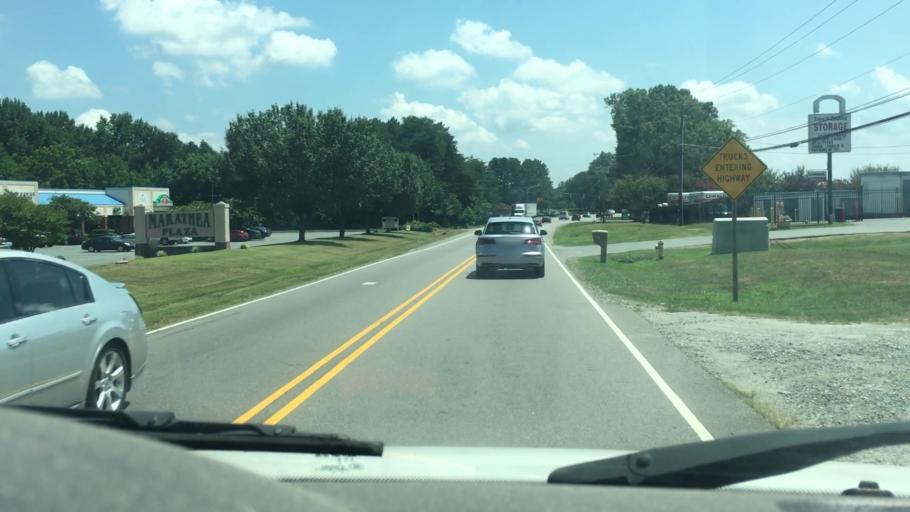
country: US
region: North Carolina
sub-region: Iredell County
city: Mooresville
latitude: 35.5817
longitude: -80.8399
